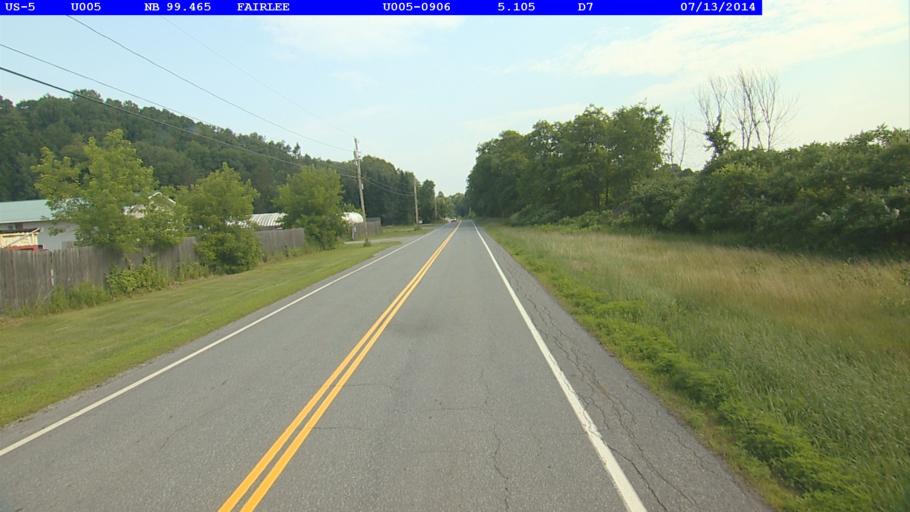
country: US
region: New Hampshire
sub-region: Grafton County
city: Orford
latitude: 43.9306
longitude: -72.1210
